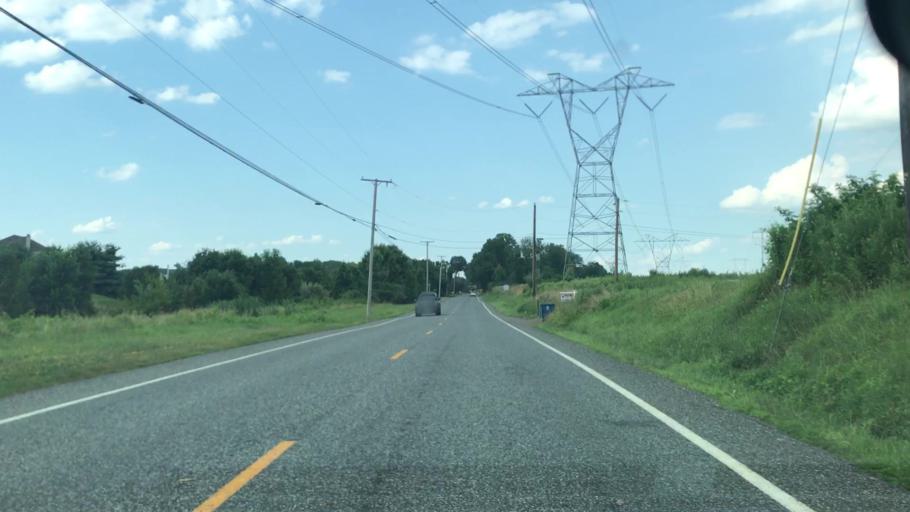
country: US
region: New Jersey
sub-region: Hunterdon County
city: Flemington
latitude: 40.4942
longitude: -74.8103
